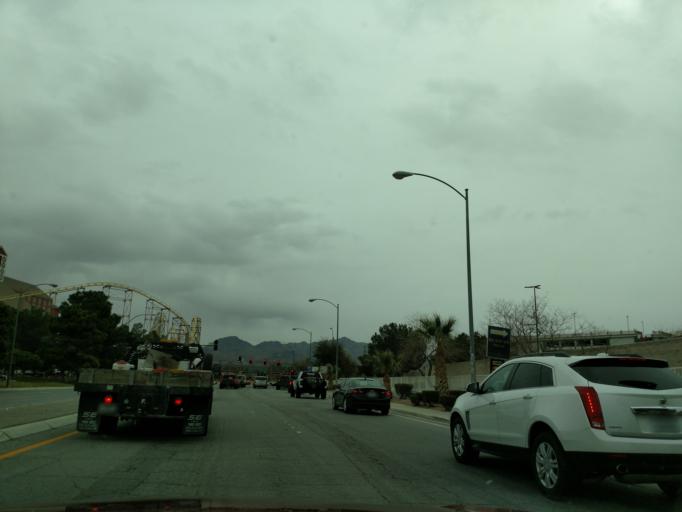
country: US
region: Nevada
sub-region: Clark County
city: Sandy Valley
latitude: 35.6123
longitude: -115.3877
